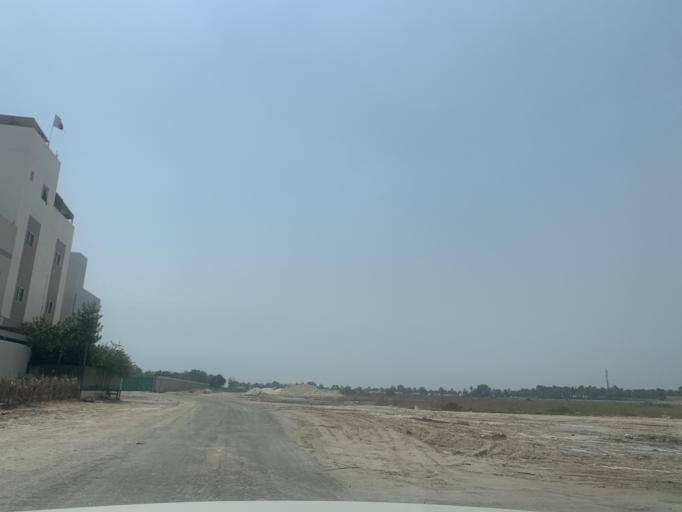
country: BH
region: Central Governorate
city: Madinat Hamad
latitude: 26.1330
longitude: 50.4670
